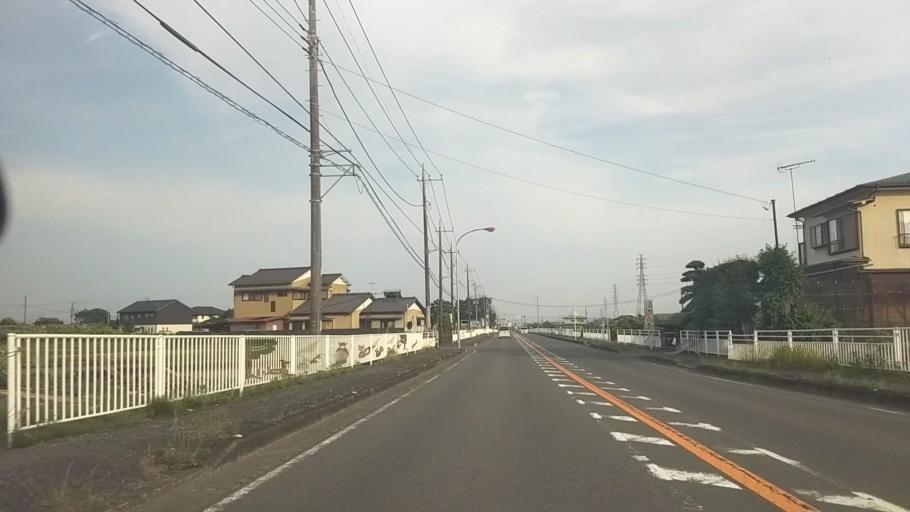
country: JP
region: Kanagawa
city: Odawara
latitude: 35.3420
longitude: 139.1016
